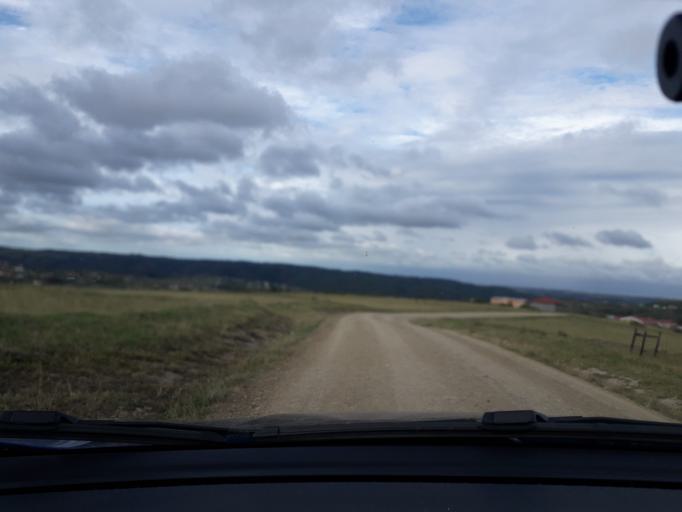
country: ZA
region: Eastern Cape
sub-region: Buffalo City Metropolitan Municipality
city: East London
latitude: -32.8040
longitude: 27.9531
